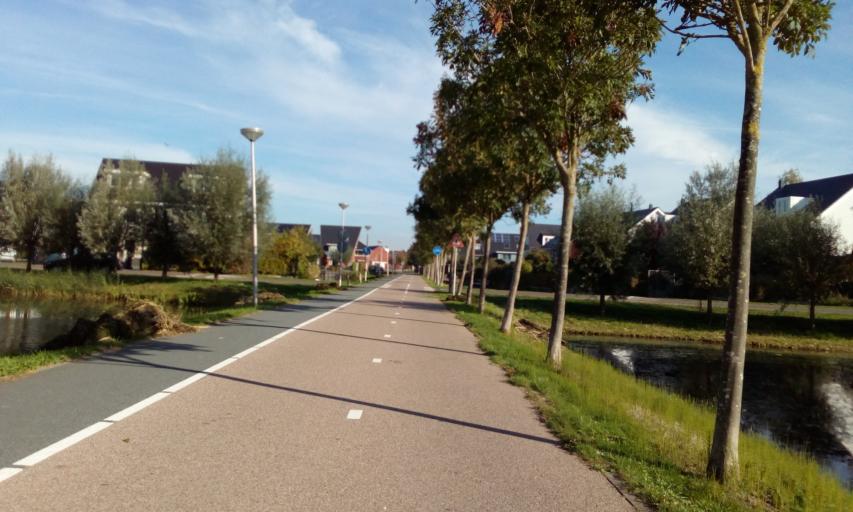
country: NL
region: Utrecht
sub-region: Stichtse Vecht
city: Spechtenkamp
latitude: 52.0974
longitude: 5.0039
